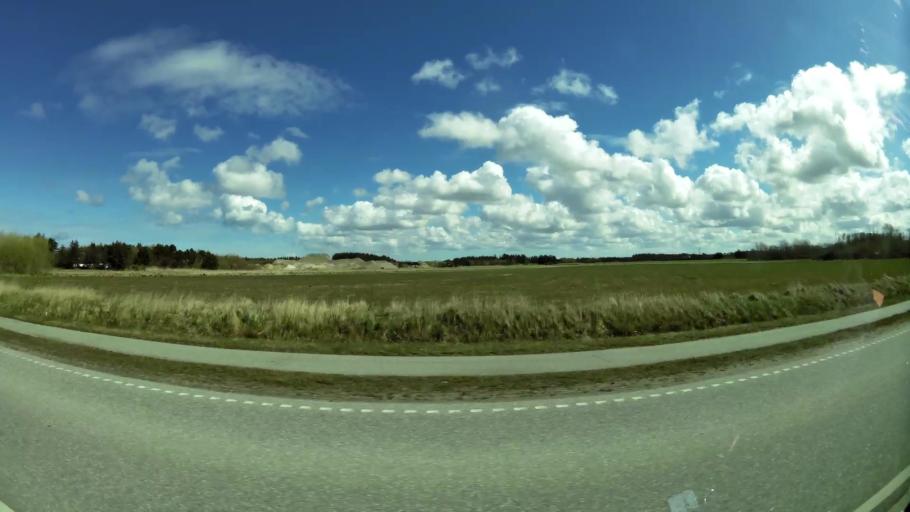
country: DK
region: North Denmark
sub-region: Hjorring Kommune
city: Hirtshals
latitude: 57.5529
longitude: 9.9388
